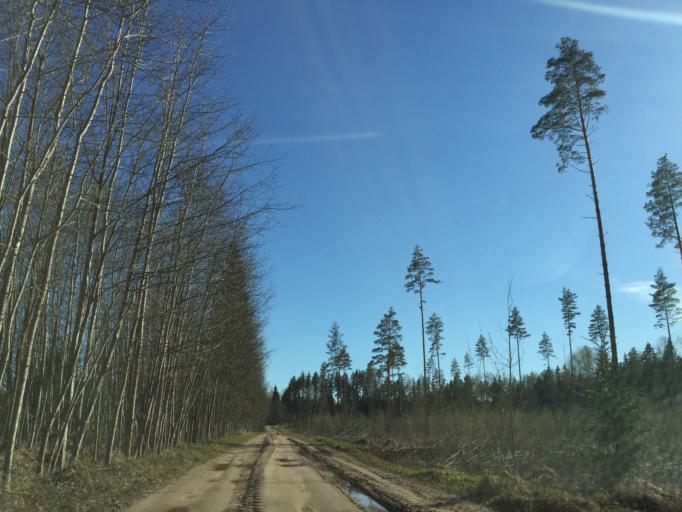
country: EE
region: Valgamaa
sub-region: Valga linn
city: Valga
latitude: 57.7796
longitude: 26.2331
